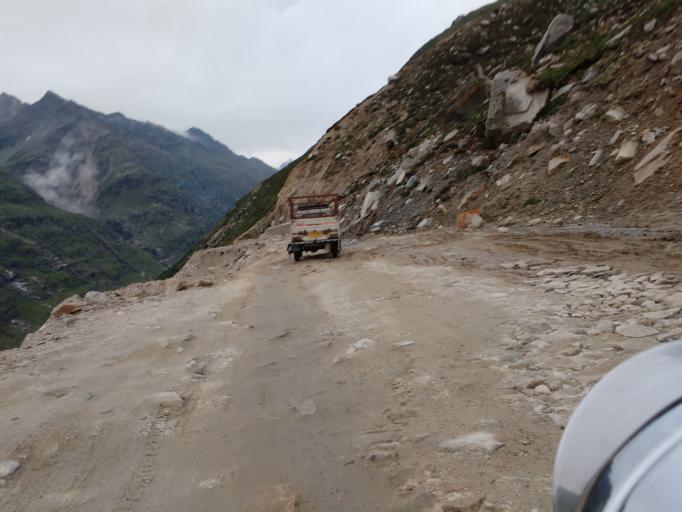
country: IN
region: Himachal Pradesh
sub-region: Kulu
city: Manali
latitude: 32.3789
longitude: 77.2666
